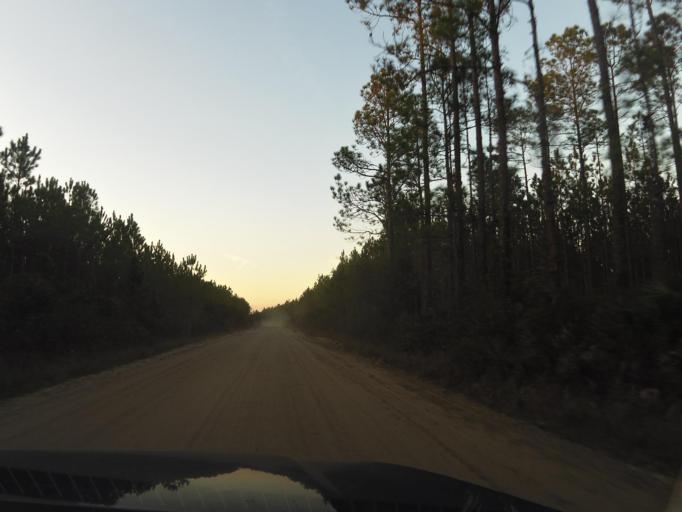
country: US
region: Florida
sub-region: Clay County
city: Asbury Lake
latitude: 29.9382
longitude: -81.7854
